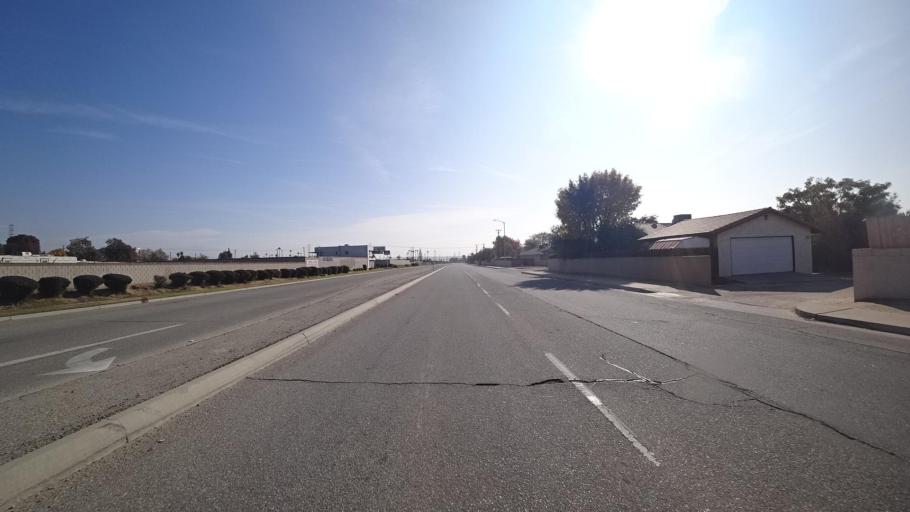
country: US
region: California
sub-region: Kern County
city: Oildale
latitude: 35.4472
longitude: -119.0288
